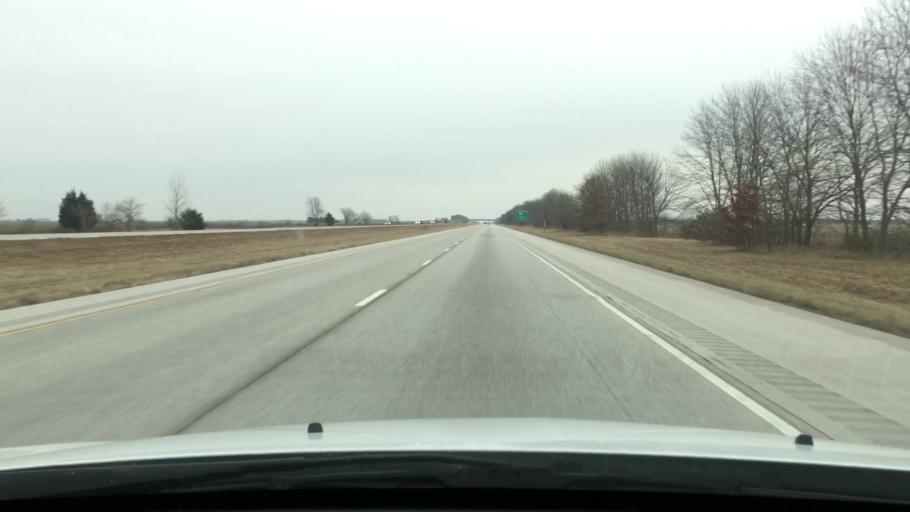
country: US
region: Illinois
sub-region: Morgan County
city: South Jacksonville
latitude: 39.6802
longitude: -90.3454
